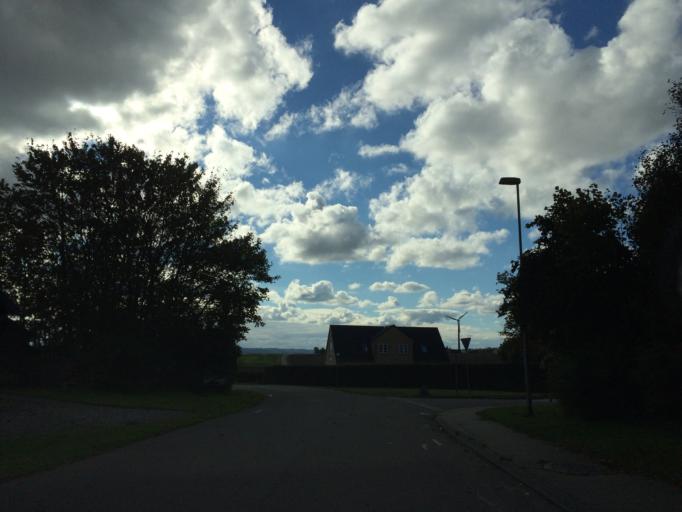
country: DK
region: Central Jutland
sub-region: Skanderborg Kommune
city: Ry
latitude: 56.1755
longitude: 9.7721
